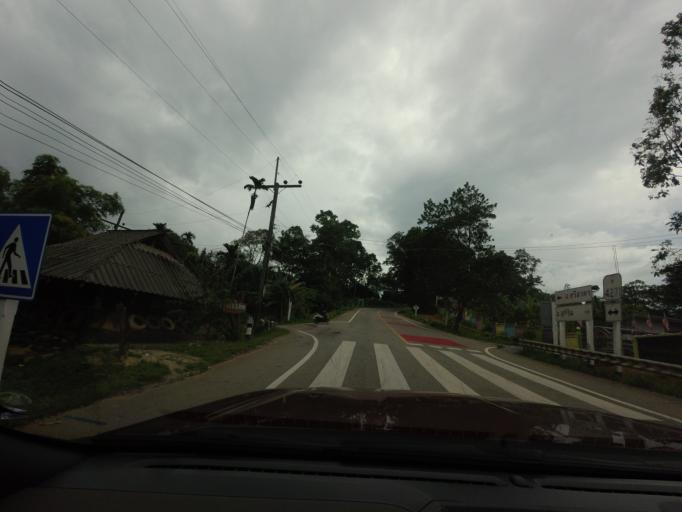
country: TH
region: Narathiwat
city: Sukhirin
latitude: 5.9787
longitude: 101.7034
